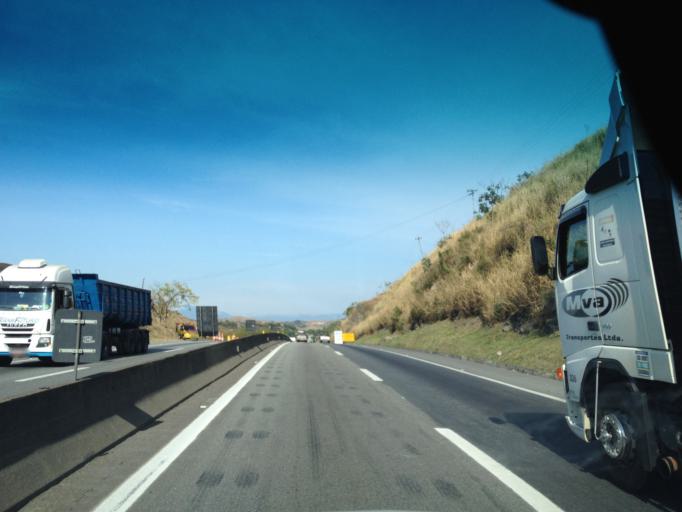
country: BR
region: Rio de Janeiro
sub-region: Barra Mansa
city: Barra Mansa
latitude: -22.5566
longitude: -44.1318
